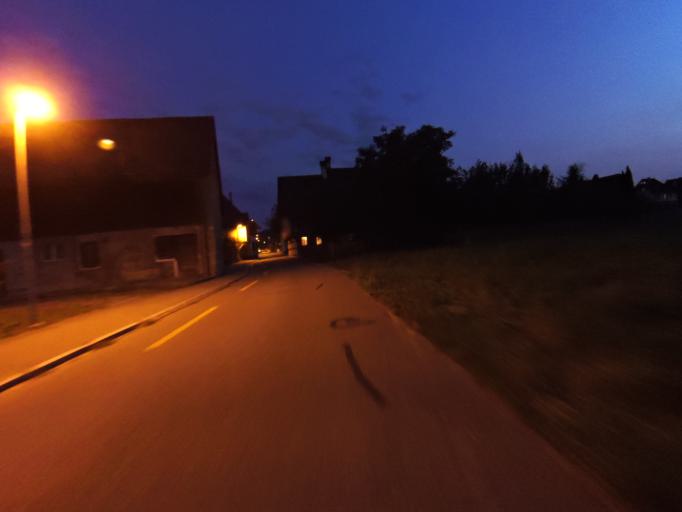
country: CH
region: Thurgau
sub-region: Frauenfeld District
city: Frauenfeld
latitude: 47.5585
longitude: 8.8898
